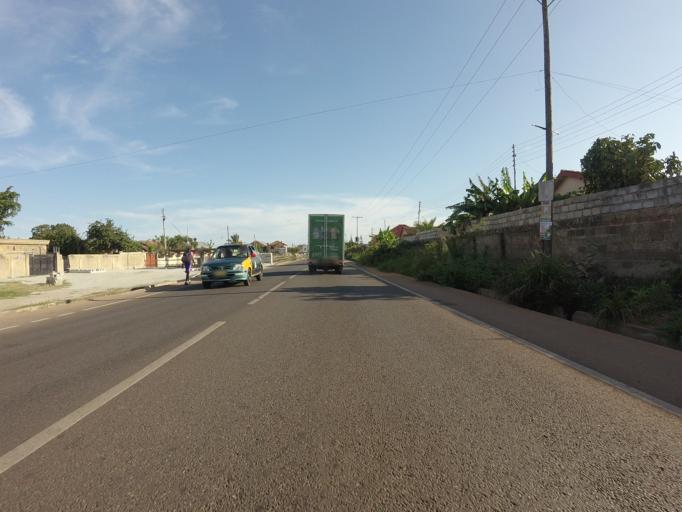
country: GH
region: Greater Accra
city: Nungua
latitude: 5.6436
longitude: -0.0926
